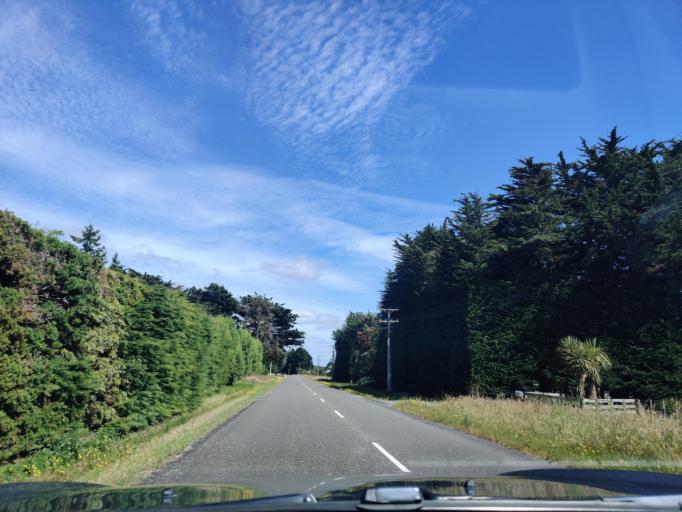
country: NZ
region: Manawatu-Wanganui
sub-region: Rangitikei District
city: Bulls
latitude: -40.1891
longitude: 175.4589
